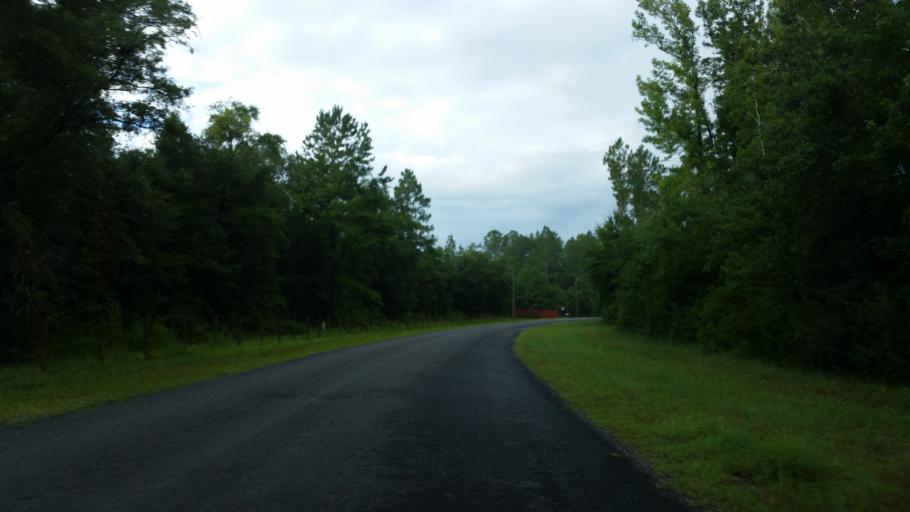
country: US
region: Florida
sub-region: Okaloosa County
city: Crestview
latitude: 30.6794
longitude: -86.7486
